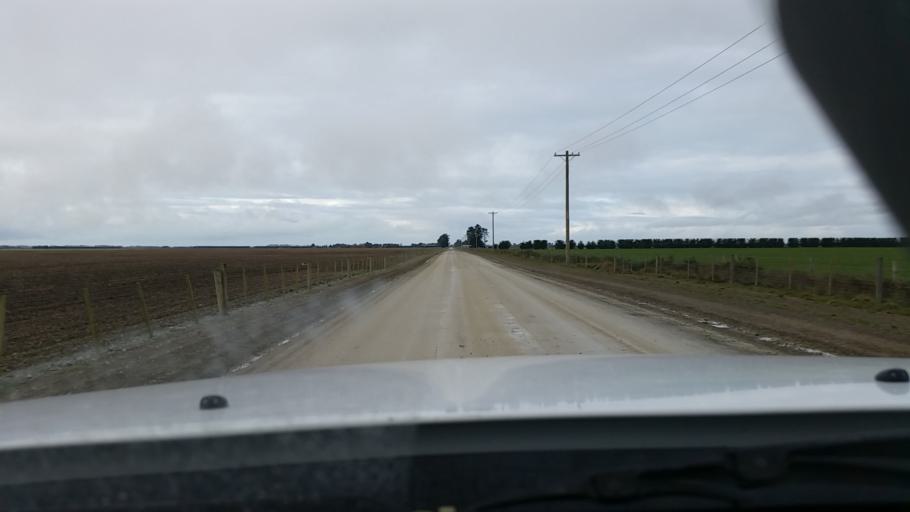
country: NZ
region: Canterbury
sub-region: Timaru District
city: Pleasant Point
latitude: -44.1273
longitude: 171.4015
